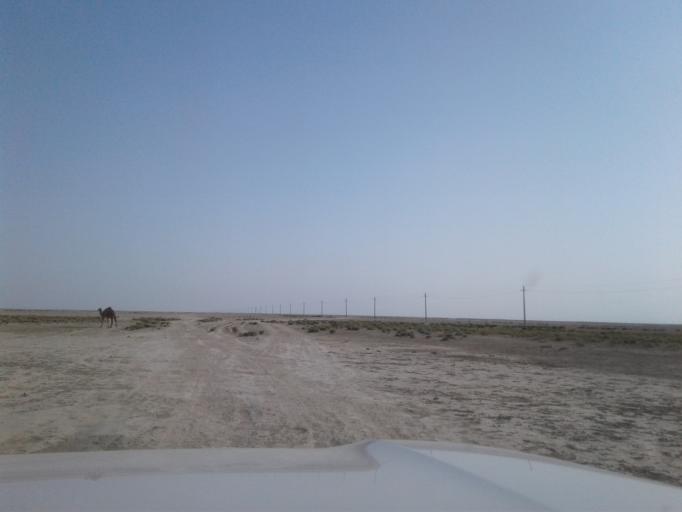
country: IR
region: Golestan
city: Aq Qayeh
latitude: 37.9958
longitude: 54.7407
